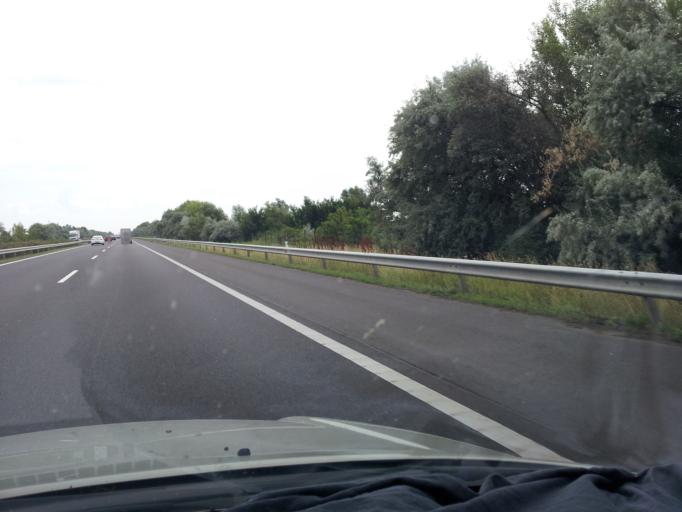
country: HU
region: Heves
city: Fuzesabony
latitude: 47.7296
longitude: 20.3791
